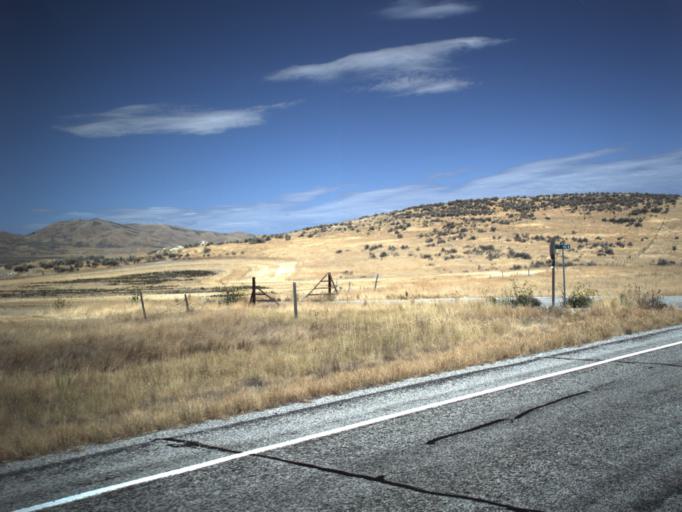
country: US
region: Utah
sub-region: Box Elder County
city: Tremonton
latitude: 41.7154
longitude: -112.4524
